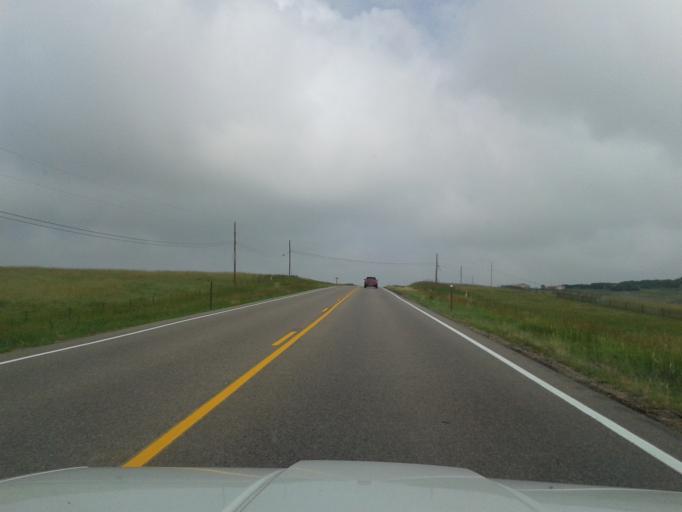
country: US
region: Colorado
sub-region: Elbert County
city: Elizabeth
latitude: 39.2674
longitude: -104.7275
